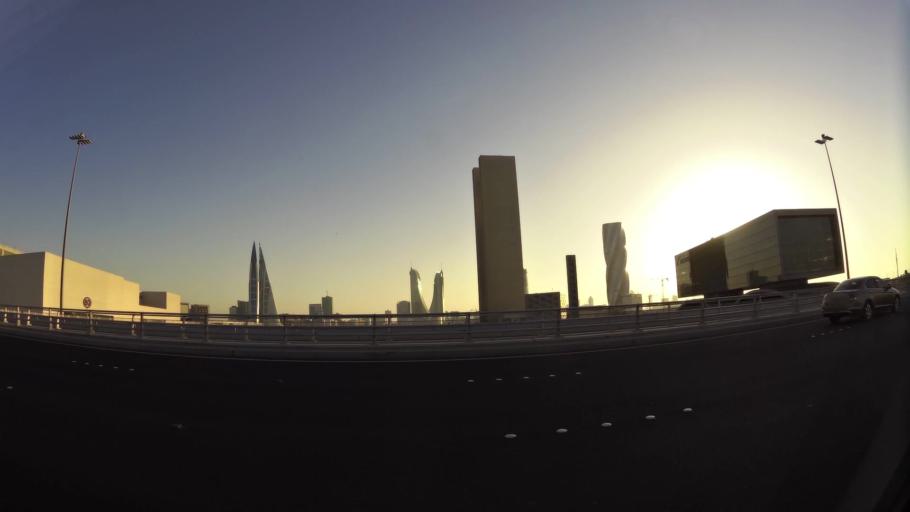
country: BH
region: Muharraq
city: Al Muharraq
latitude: 26.2501
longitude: 50.5857
